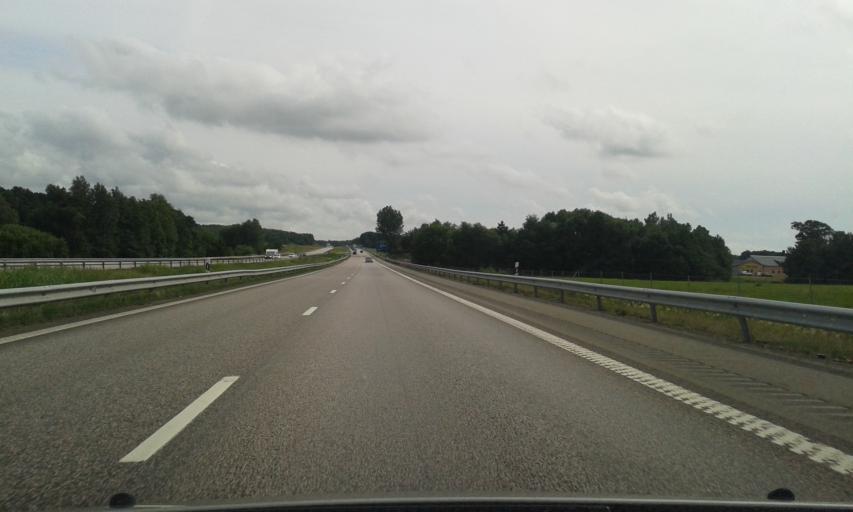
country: SE
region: Halland
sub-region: Kungsbacka Kommun
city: Frillesas
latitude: 57.2625
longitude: 12.2157
